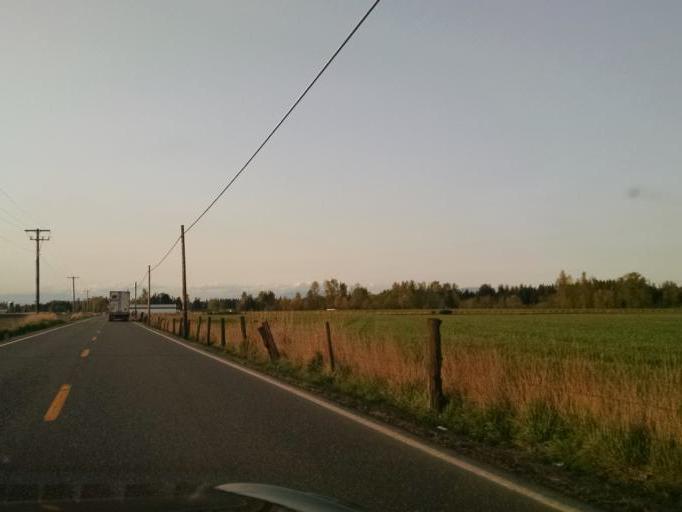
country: US
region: Washington
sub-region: Whatcom County
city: Nooksack
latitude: 48.8998
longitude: -122.3206
